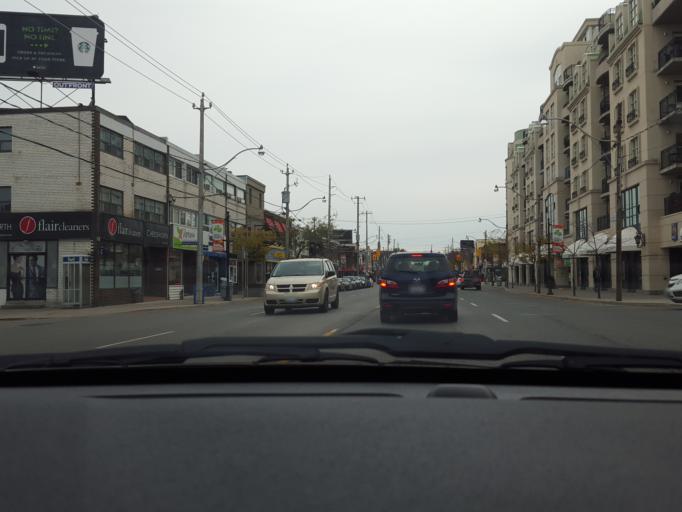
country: CA
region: Ontario
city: Toronto
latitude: 43.7066
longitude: -79.3893
